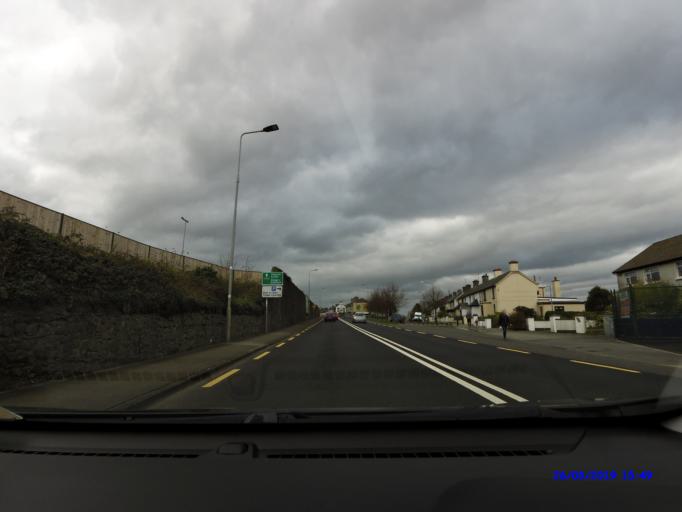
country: IE
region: Connaught
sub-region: Maigh Eo
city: Ballina
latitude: 54.1072
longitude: -9.1624
